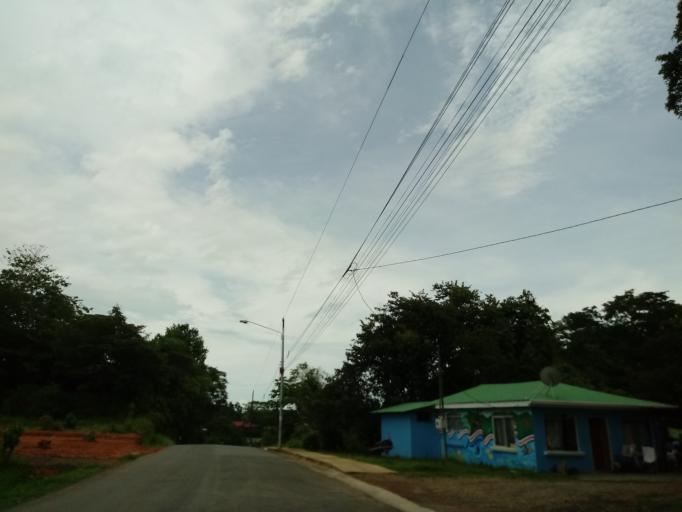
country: CR
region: San Jose
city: Mercedes
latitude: 9.1608
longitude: -83.7369
